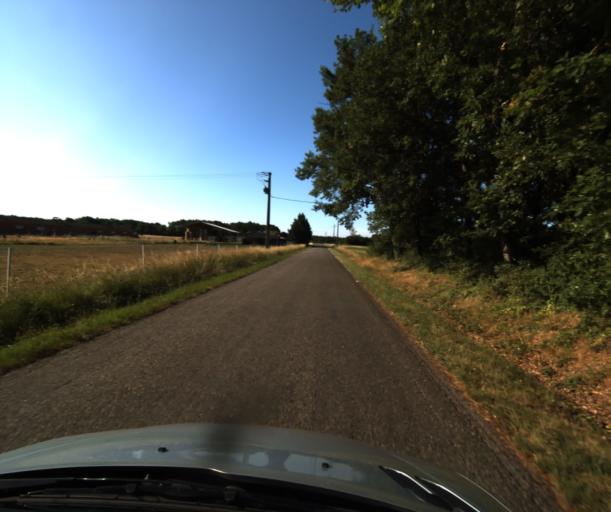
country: FR
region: Midi-Pyrenees
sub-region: Departement du Tarn-et-Garonne
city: Saint-Porquier
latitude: 44.0608
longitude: 1.2082
